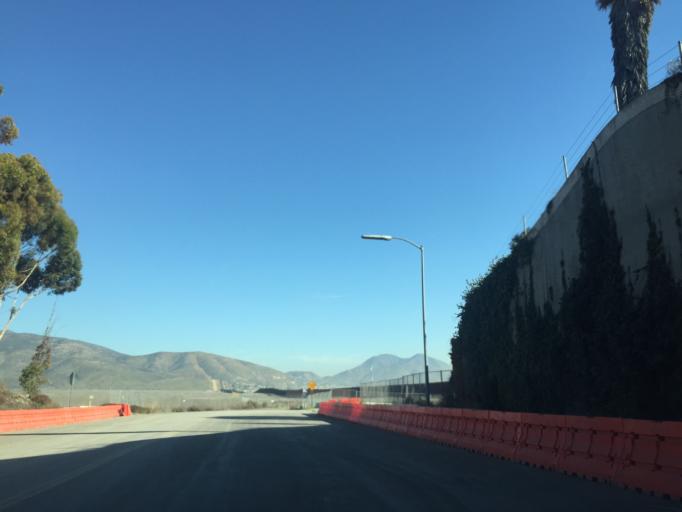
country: MX
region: Baja California
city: Tijuana
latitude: 32.5527
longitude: -116.9267
